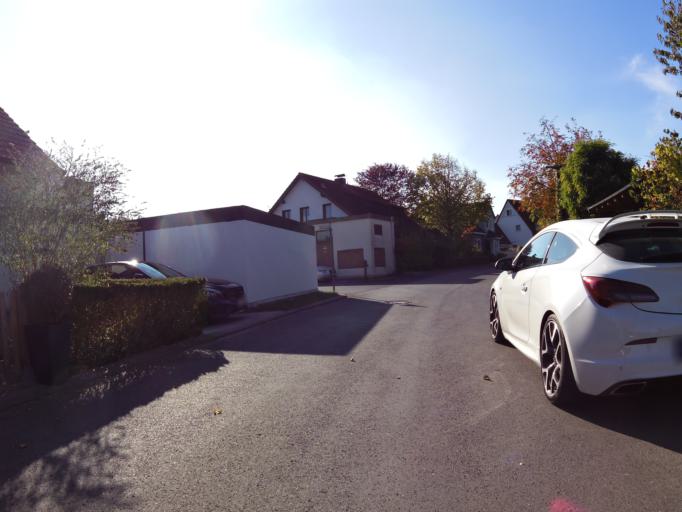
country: DE
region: Bavaria
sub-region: Regierungsbezirk Unterfranken
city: Winterhausen
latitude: 49.7036
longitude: 10.0137
